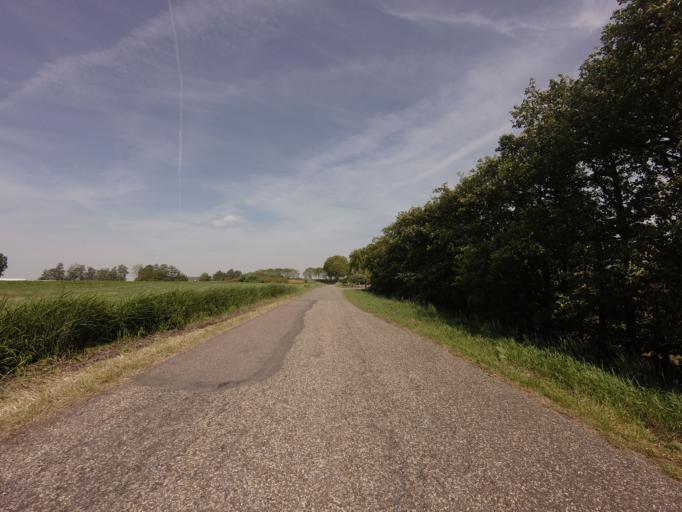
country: NL
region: Utrecht
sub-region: Gemeente De Ronde Venen
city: Mijdrecht
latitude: 52.2270
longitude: 4.8879
